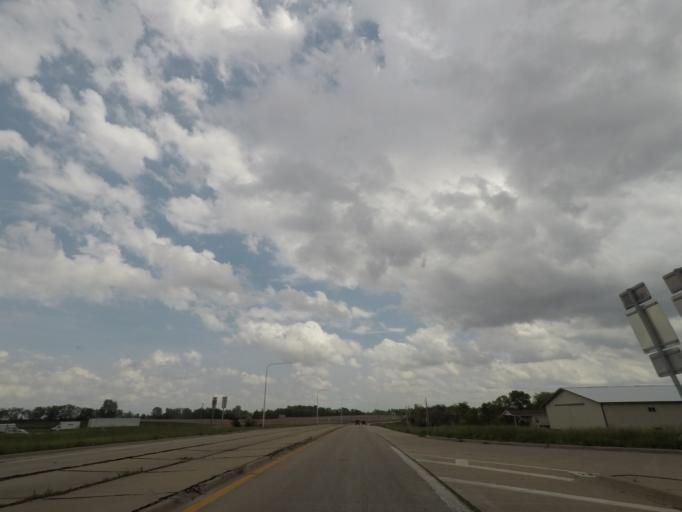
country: US
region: Illinois
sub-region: De Witt County
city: Clinton
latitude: 40.1747
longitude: -88.9625
